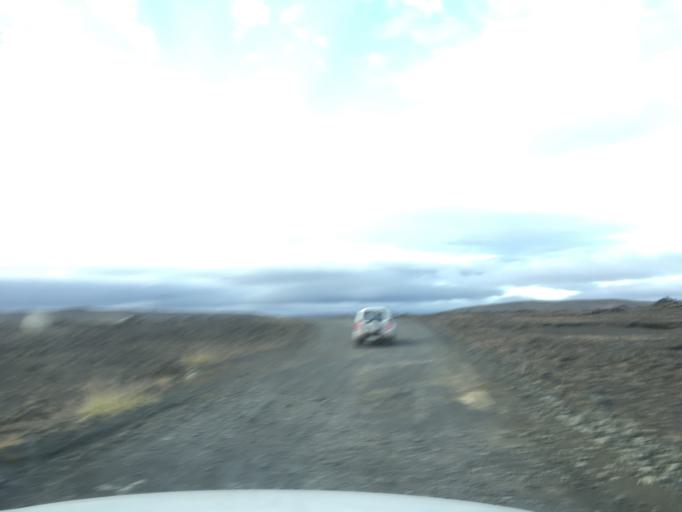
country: IS
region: South
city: Vestmannaeyjar
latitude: 64.1428
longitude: -19.1291
